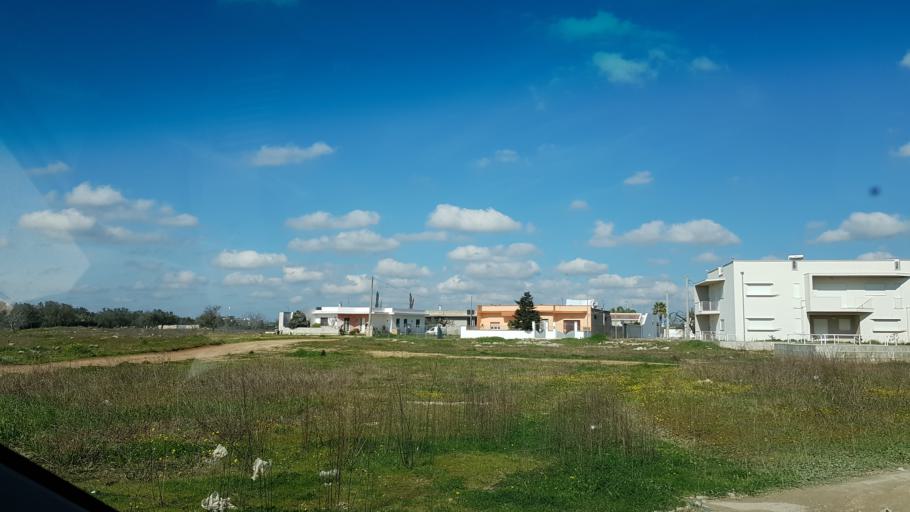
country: IT
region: Apulia
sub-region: Provincia di Lecce
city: Veglie
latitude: 40.3403
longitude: 17.9598
